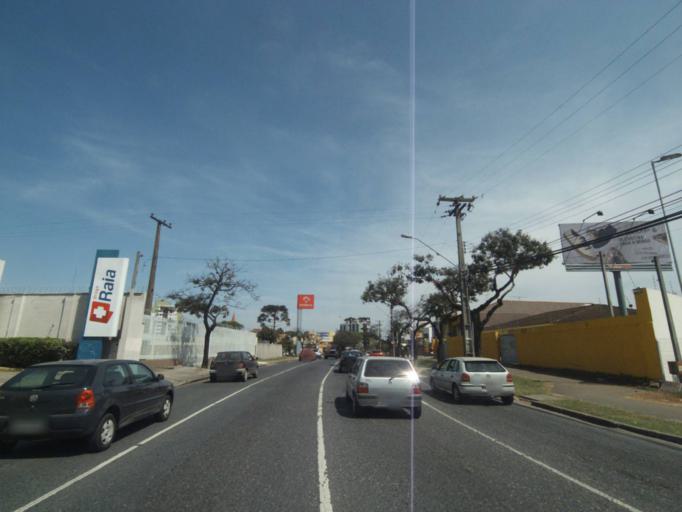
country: BR
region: Parana
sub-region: Curitiba
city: Curitiba
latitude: -25.4709
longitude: -49.2952
